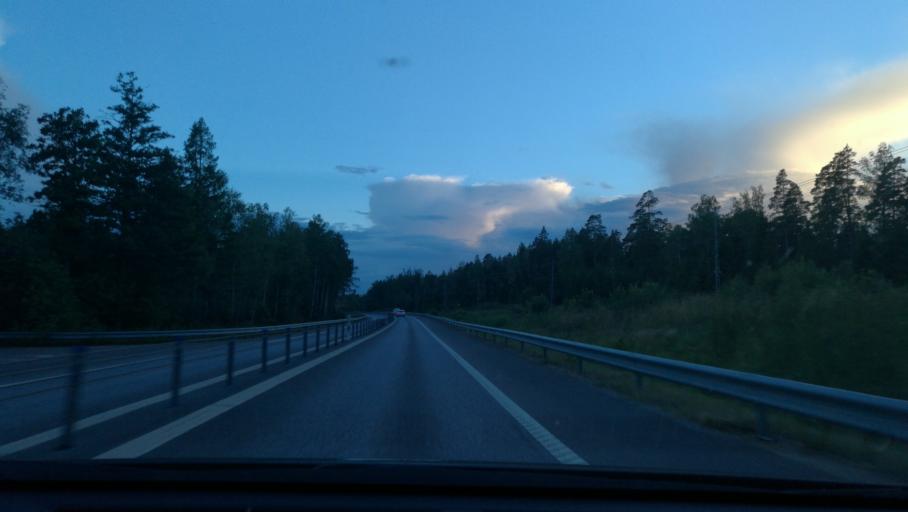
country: SE
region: OEstergoetland
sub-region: Norrkopings Kommun
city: Jursla
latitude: 58.8165
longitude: 16.1593
